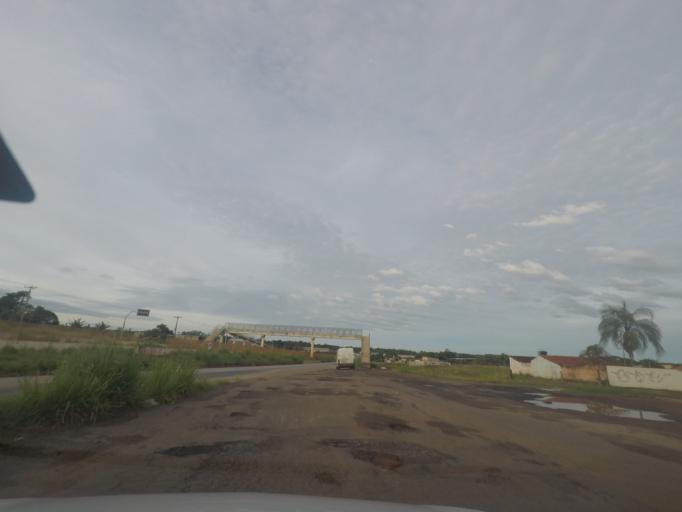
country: BR
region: Goias
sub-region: Trindade
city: Trindade
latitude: -16.7250
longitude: -49.3794
